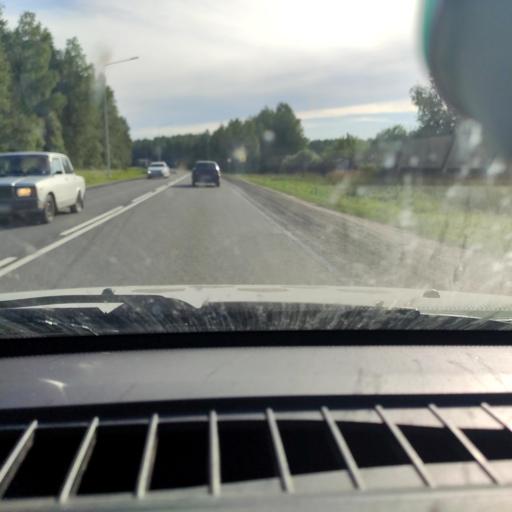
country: RU
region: Kirov
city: Vakhrushi
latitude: 58.6671
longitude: 49.9327
